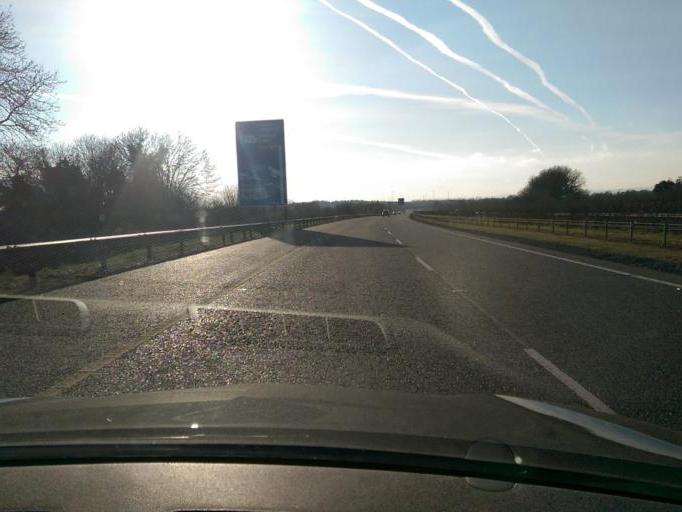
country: IE
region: Leinster
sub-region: Laois
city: Portlaoise
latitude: 53.0136
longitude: -7.2829
